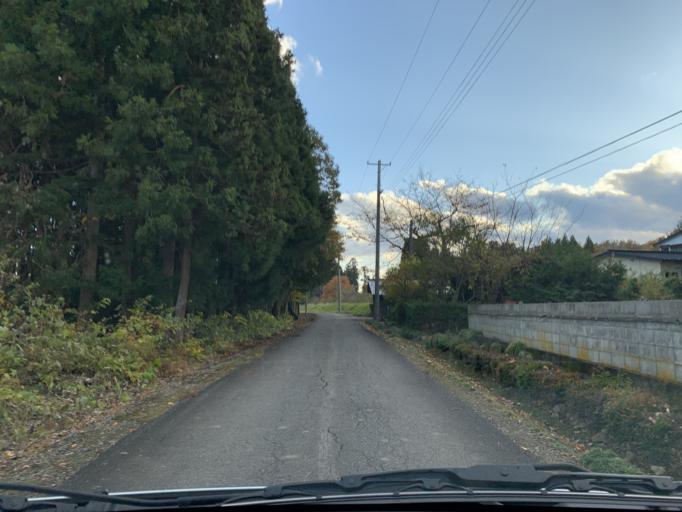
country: JP
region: Iwate
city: Mizusawa
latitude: 39.1084
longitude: 141.0394
